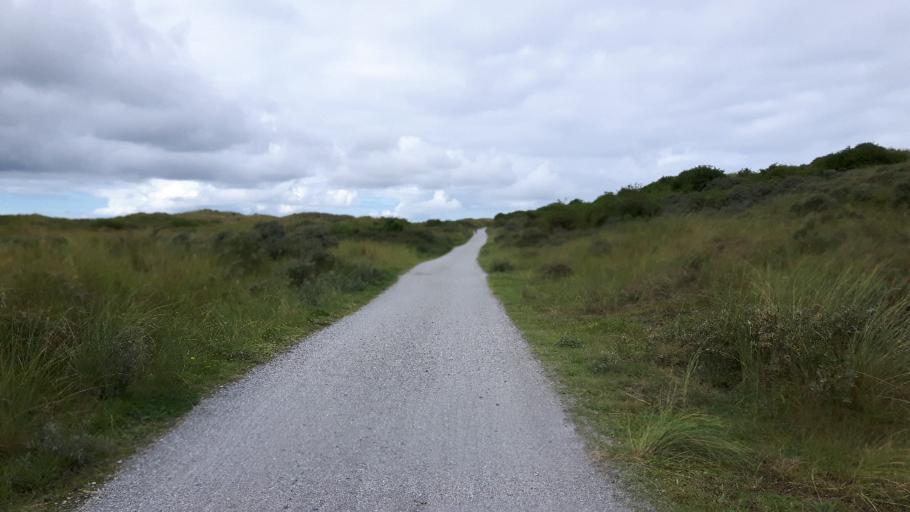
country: NL
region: Friesland
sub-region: Gemeente Ameland
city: Nes
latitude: 53.4575
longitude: 5.7291
